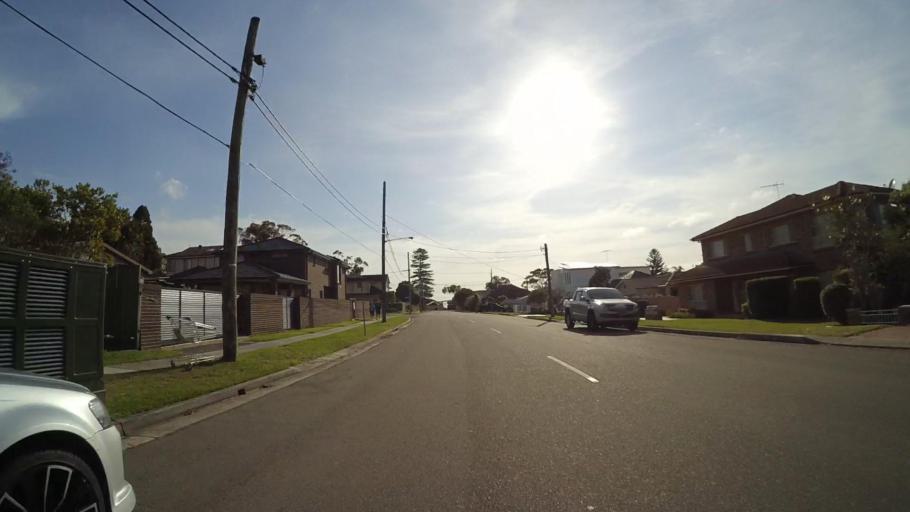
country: AU
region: New South Wales
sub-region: Kogarah
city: Blakehurst
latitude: -34.0116
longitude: 151.1123
